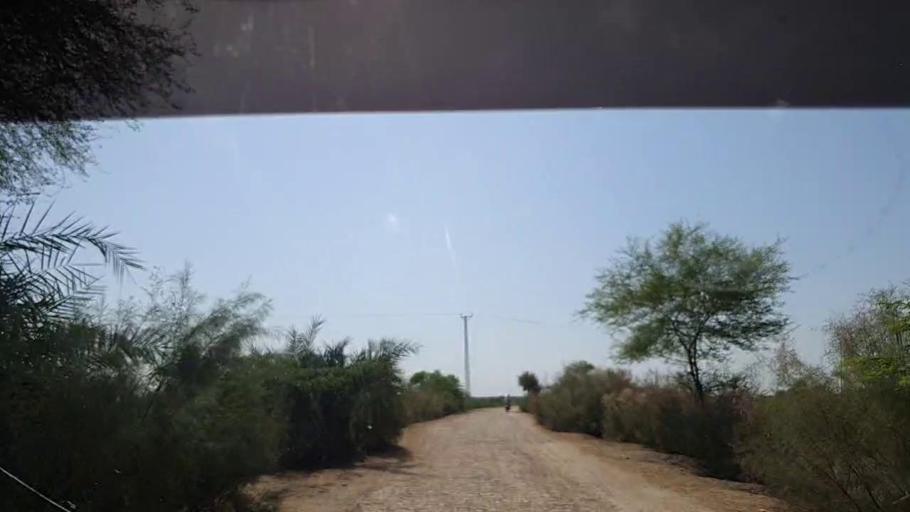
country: PK
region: Sindh
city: Ghauspur
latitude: 28.2168
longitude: 69.0922
